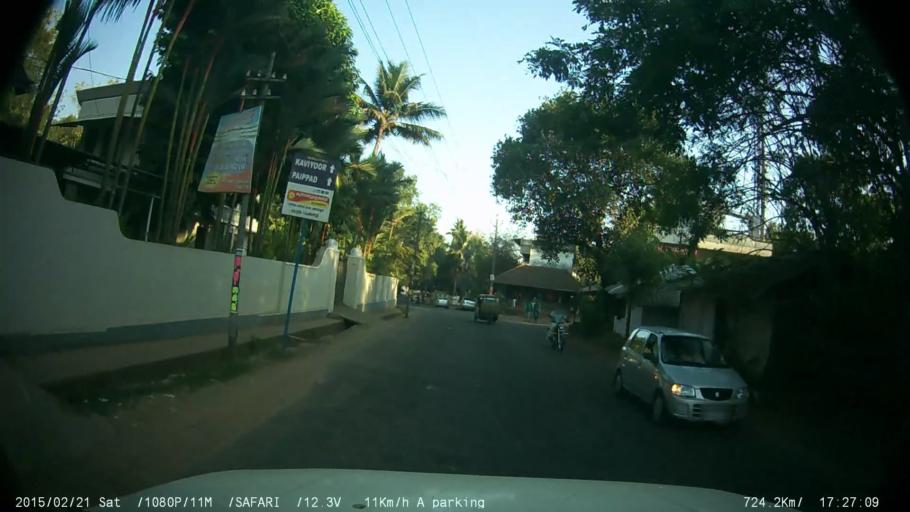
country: IN
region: Kerala
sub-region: Kottayam
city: Changanacheri
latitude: 9.4446
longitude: 76.5550
